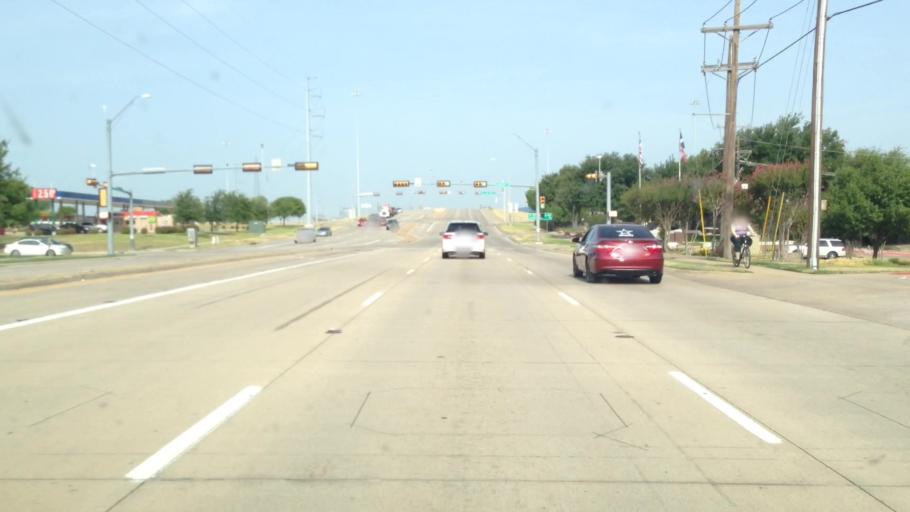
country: US
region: Texas
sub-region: Denton County
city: Lewisville
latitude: 33.0036
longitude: -96.9889
